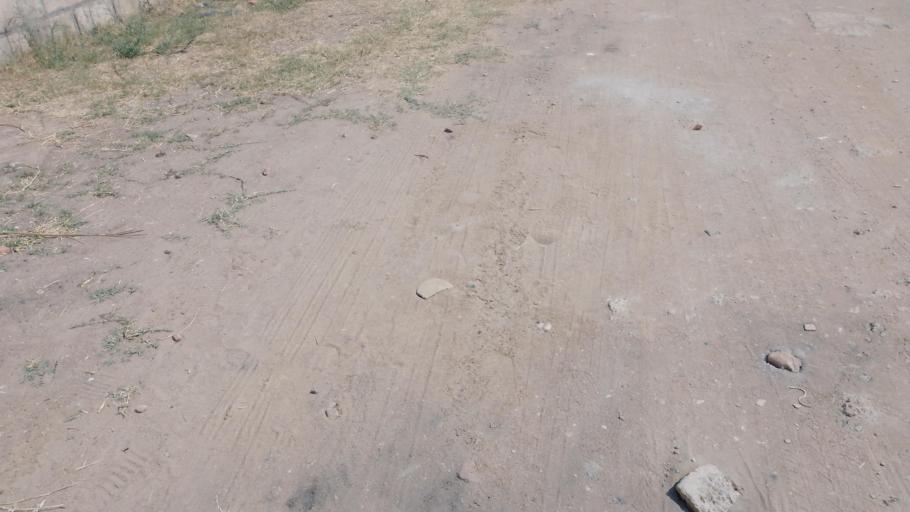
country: ZM
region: Lusaka
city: Lusaka
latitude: -15.3907
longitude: 28.3904
